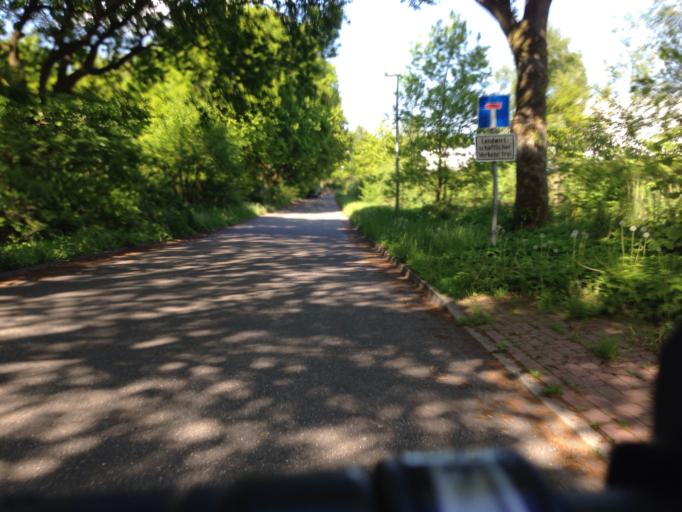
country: DE
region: Schleswig-Holstein
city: Stapelfeld
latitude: 53.6215
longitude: 10.2254
